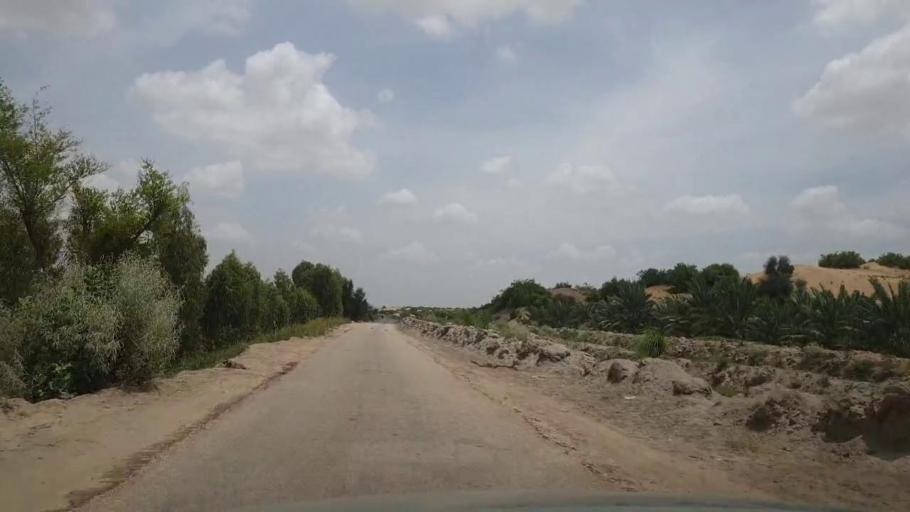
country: PK
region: Sindh
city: Kot Diji
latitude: 27.1987
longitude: 69.0708
